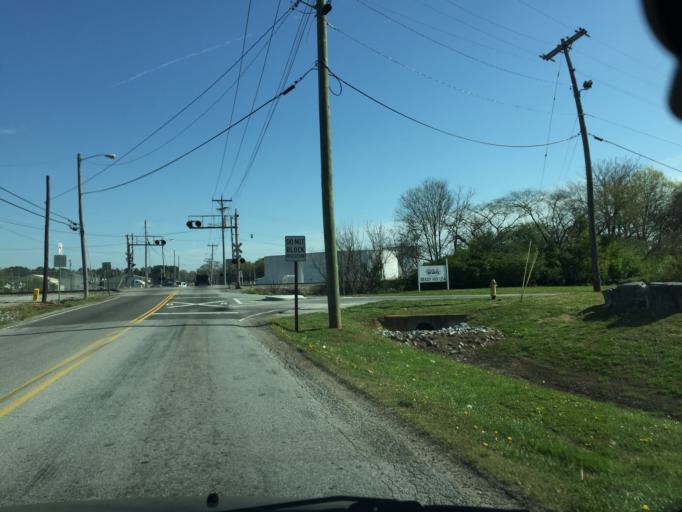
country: US
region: Tennessee
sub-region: Hamilton County
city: East Chattanooga
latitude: 35.0690
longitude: -85.1928
